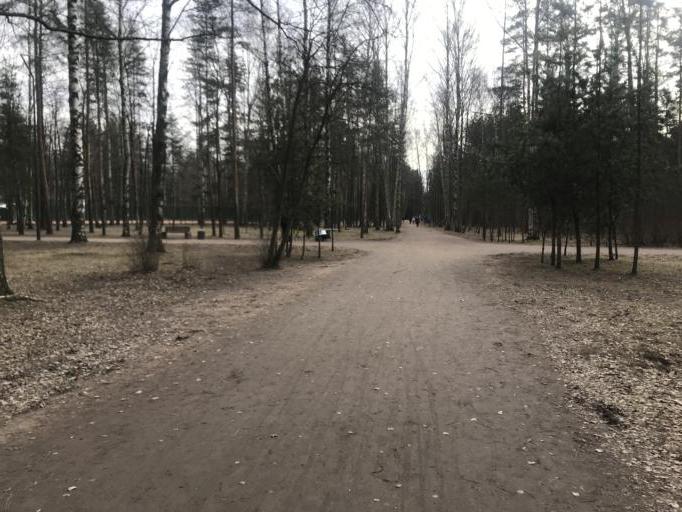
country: RU
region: St.-Petersburg
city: Sosnovka
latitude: 60.0174
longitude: 30.3472
